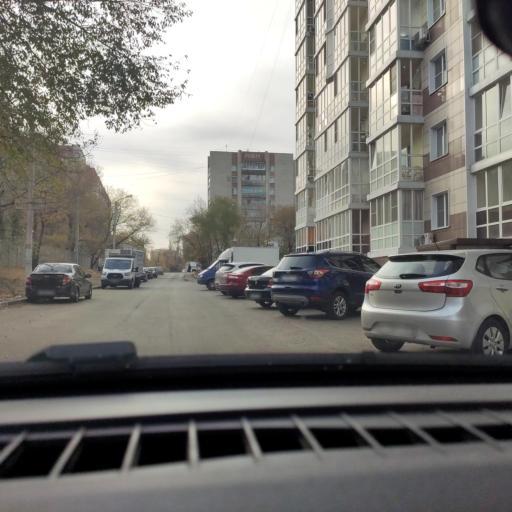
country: RU
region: Voronezj
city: Voronezh
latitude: 51.7133
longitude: 39.2709
